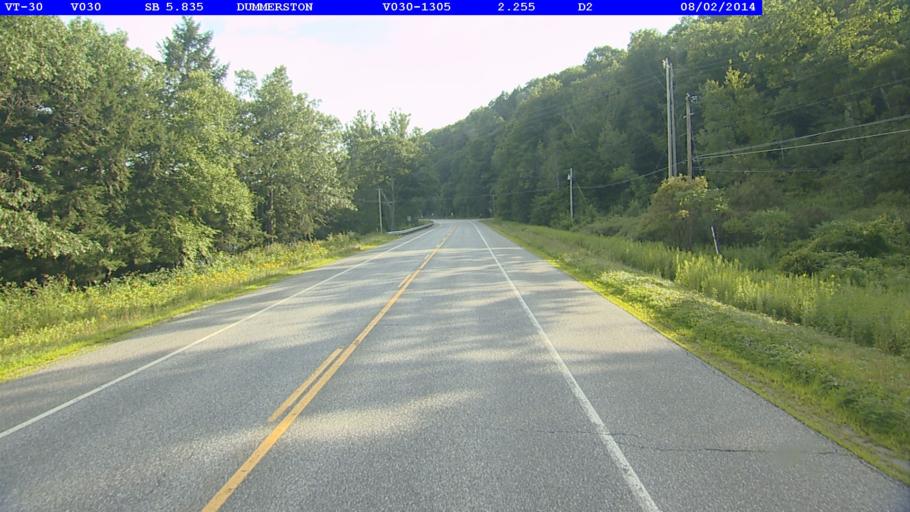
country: US
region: Vermont
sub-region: Windham County
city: West Brattleboro
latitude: 42.9254
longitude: -72.6134
